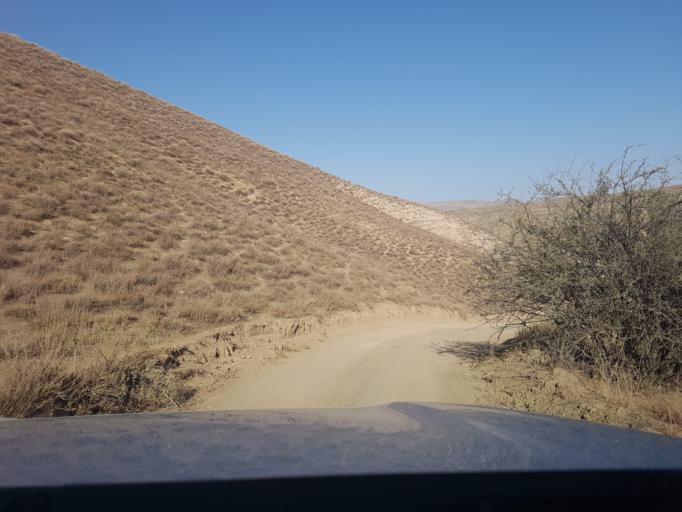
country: TM
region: Balkan
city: Magtymguly
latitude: 38.2997
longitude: 56.7836
